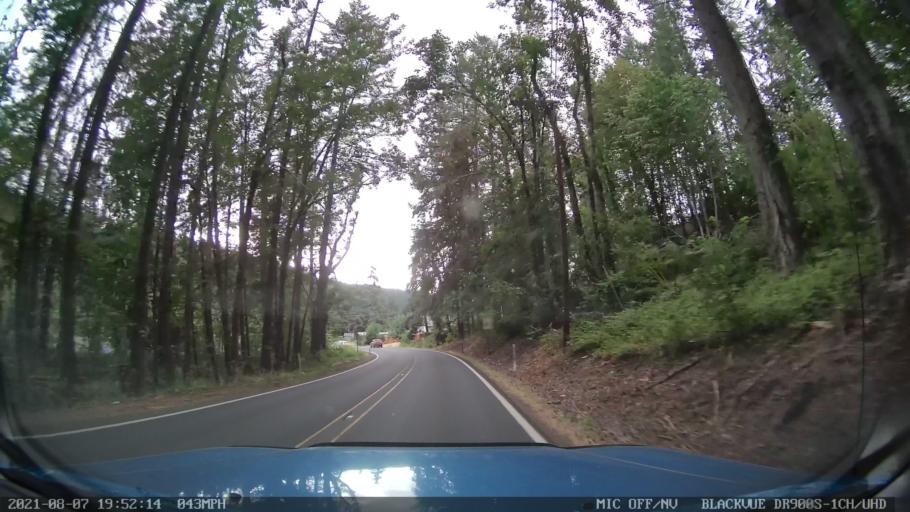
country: US
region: Oregon
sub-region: Marion County
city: Silverton
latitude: 44.9840
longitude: -122.7552
